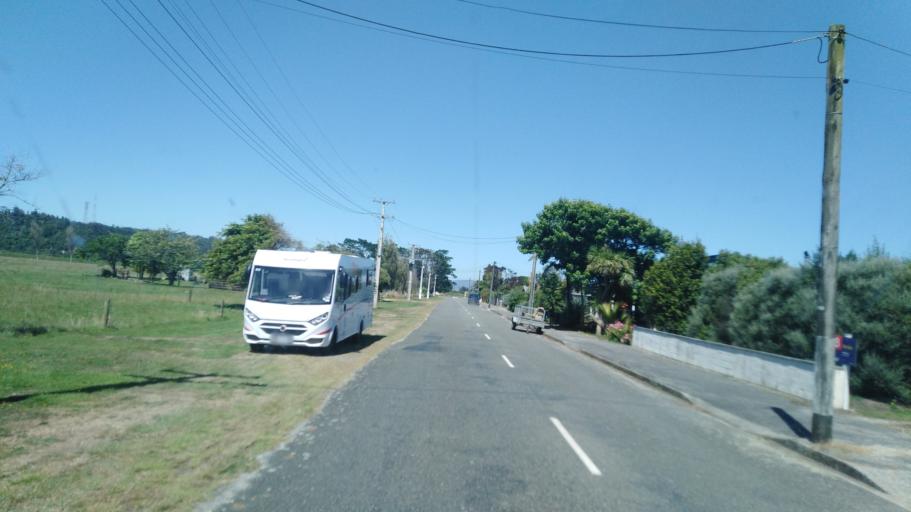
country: NZ
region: West Coast
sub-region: Buller District
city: Westport
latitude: -41.2489
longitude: 172.1111
